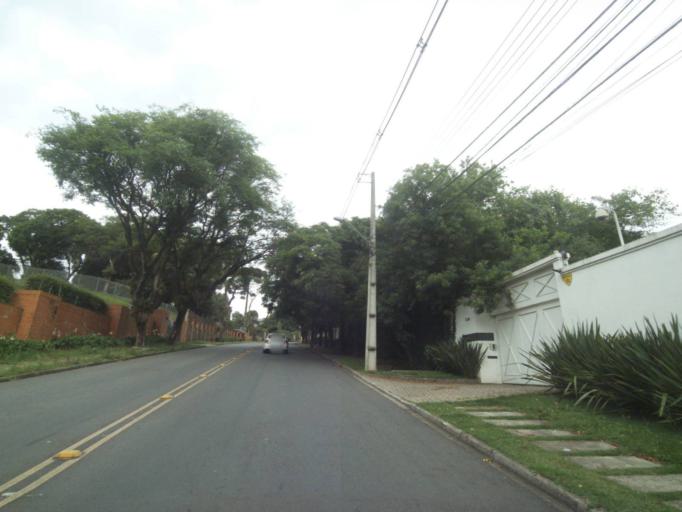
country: BR
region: Parana
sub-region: Curitiba
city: Curitiba
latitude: -25.4047
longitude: -49.3009
